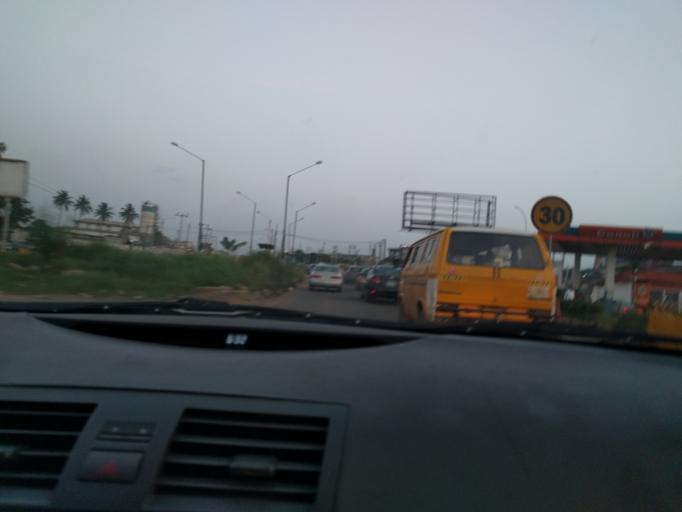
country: NG
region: Lagos
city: Oshodi
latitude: 6.5550
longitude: 3.3236
